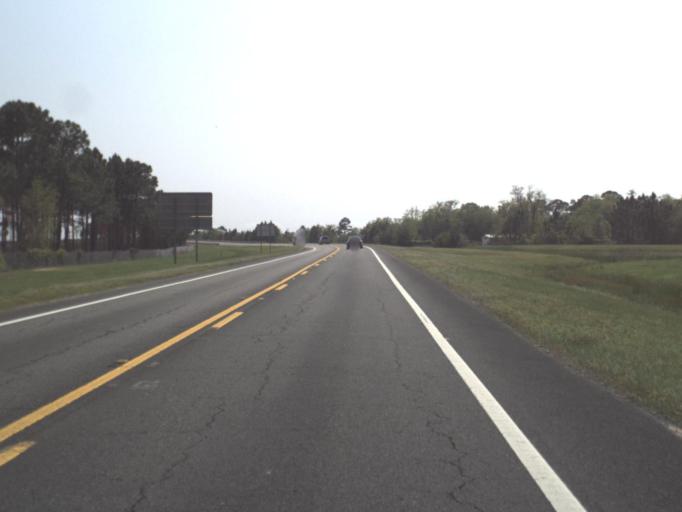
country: US
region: Florida
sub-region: Santa Rosa County
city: Oriole Beach
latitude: 30.4500
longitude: -87.0989
